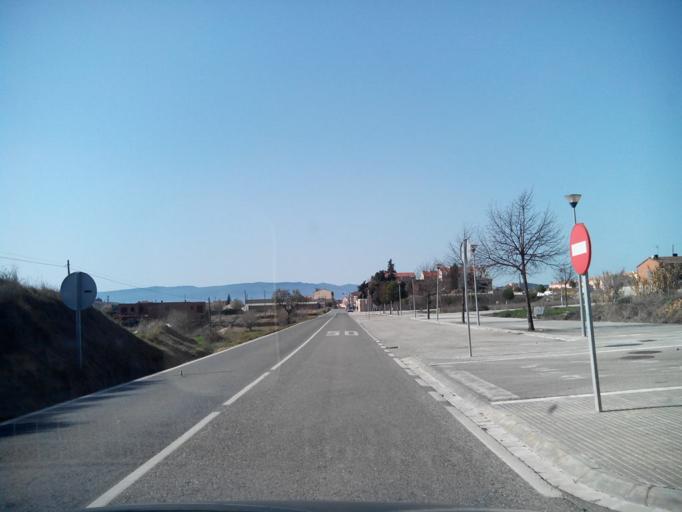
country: ES
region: Catalonia
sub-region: Provincia de Tarragona
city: Fores
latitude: 41.4494
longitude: 1.2537
